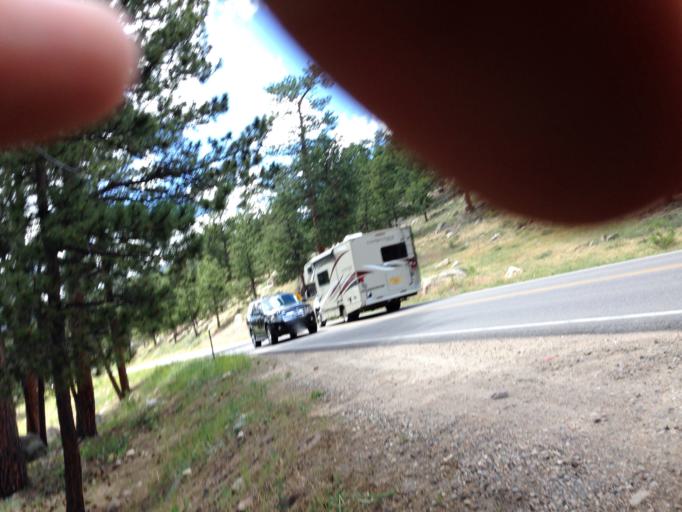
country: US
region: Colorado
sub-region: Larimer County
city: Estes Park
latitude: 40.3605
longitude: -105.5882
